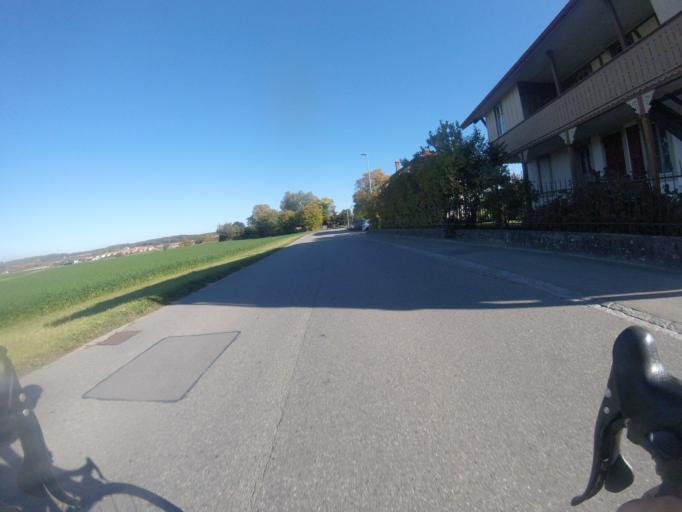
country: CH
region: Bern
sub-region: Seeland District
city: Schupfen
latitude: 47.0401
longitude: 7.3703
